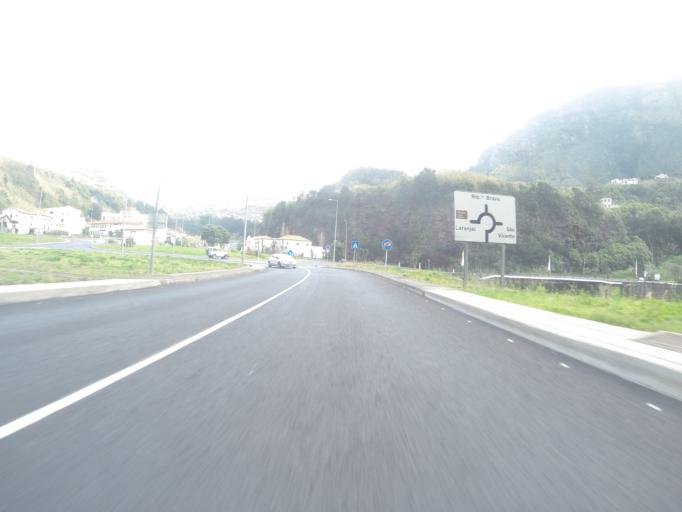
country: PT
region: Madeira
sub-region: Sao Vicente
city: Sao Vicente
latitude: 32.8031
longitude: -17.0441
